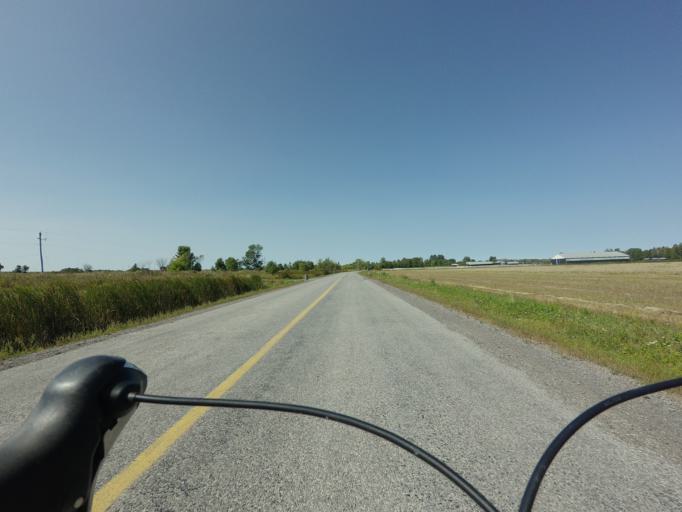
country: CA
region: Ontario
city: Arnprior
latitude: 45.4488
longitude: -76.0815
